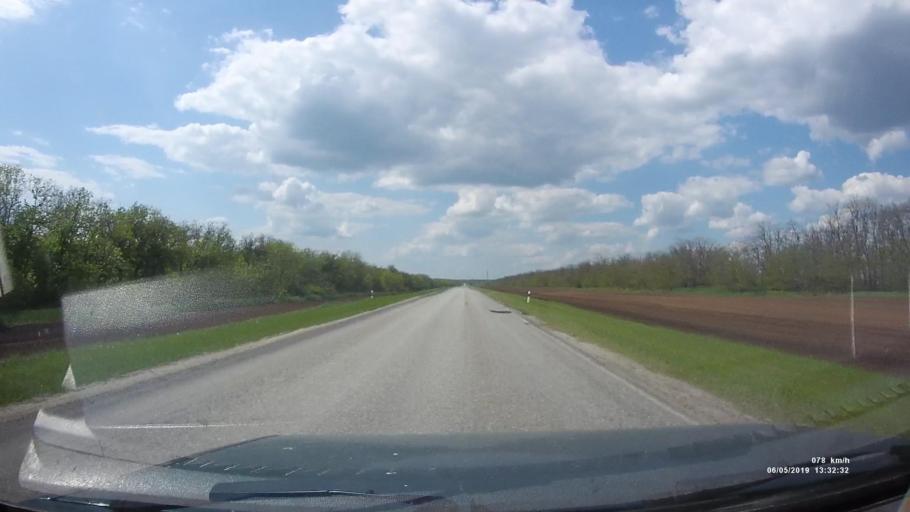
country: RU
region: Rostov
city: Ust'-Donetskiy
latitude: 47.6844
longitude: 40.7940
